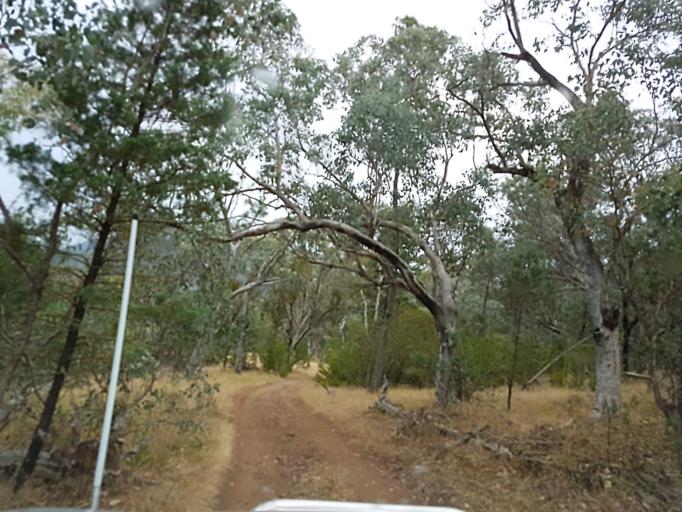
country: AU
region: New South Wales
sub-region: Snowy River
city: Jindabyne
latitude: -36.9433
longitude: 148.3952
